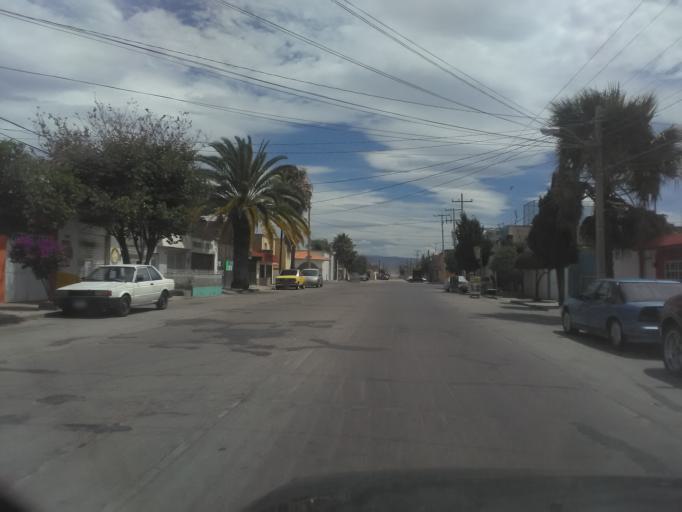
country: MX
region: Durango
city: Victoria de Durango
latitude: 24.0208
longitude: -104.6311
